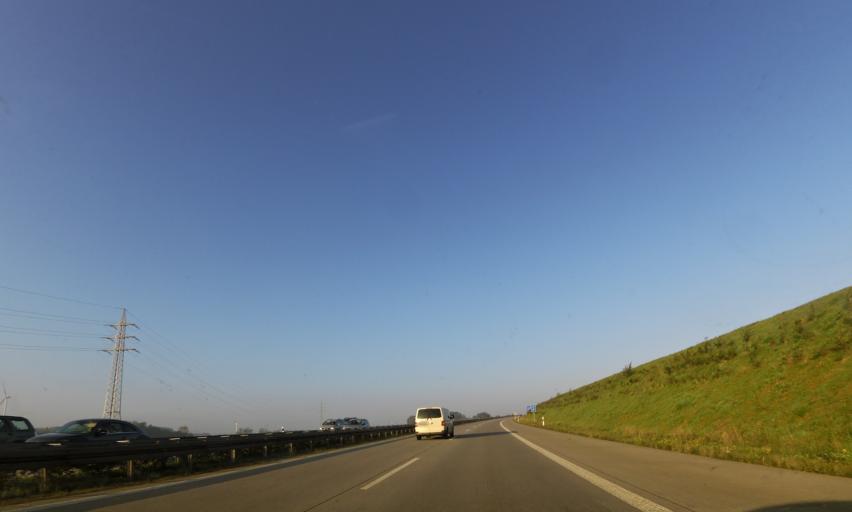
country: DE
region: Saxony
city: Oelsnitz
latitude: 50.6919
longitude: 12.7165
